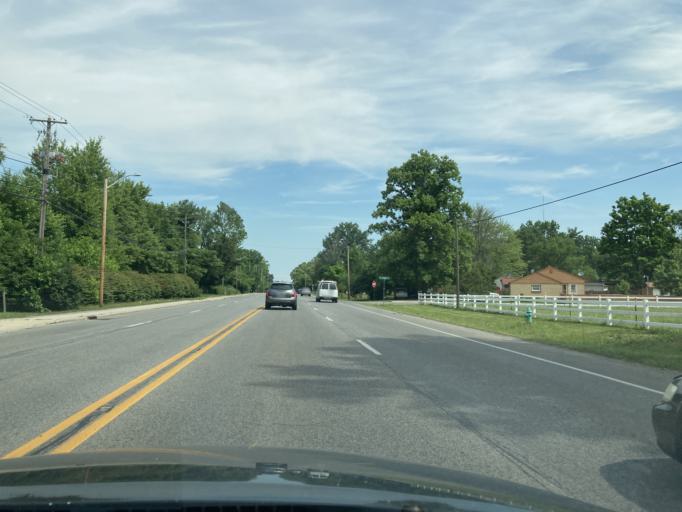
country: US
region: Indiana
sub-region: Marion County
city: Meridian Hills
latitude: 39.8720
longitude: -86.2036
